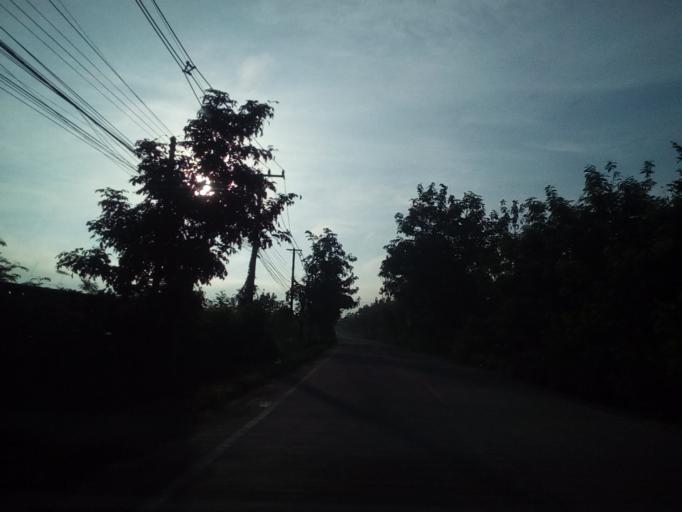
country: TH
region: Lamphun
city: Ban Thi
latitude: 18.6240
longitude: 99.0755
